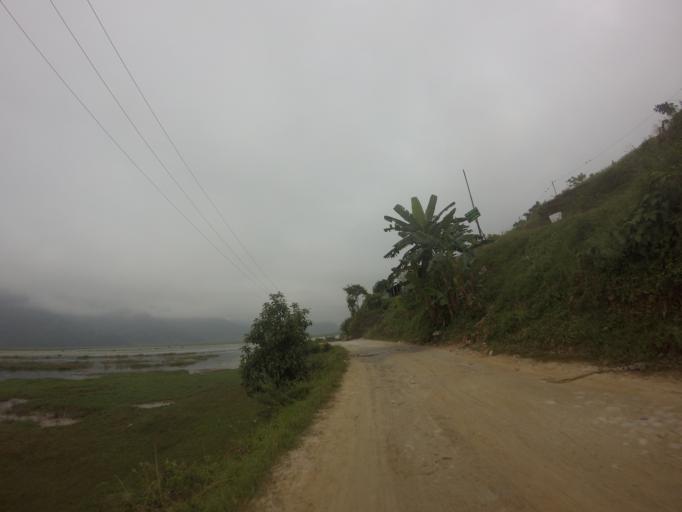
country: NP
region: Western Region
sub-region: Gandaki Zone
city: Pokhara
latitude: 28.2281
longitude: 83.9331
